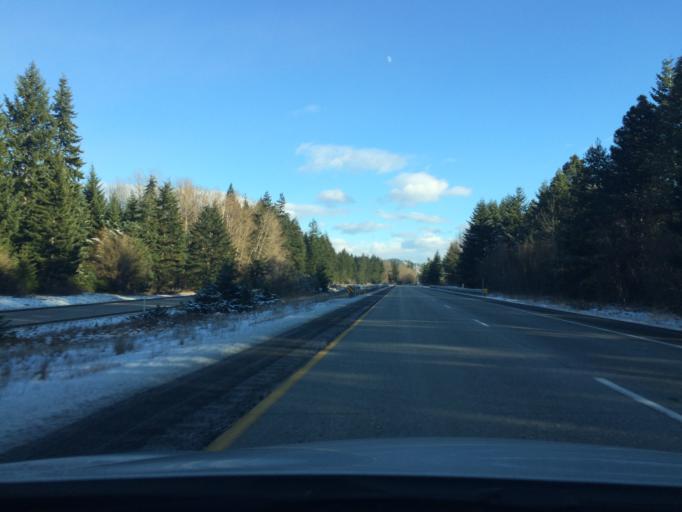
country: US
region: Washington
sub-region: Kittitas County
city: Cle Elum
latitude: 47.2145
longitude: -121.1148
